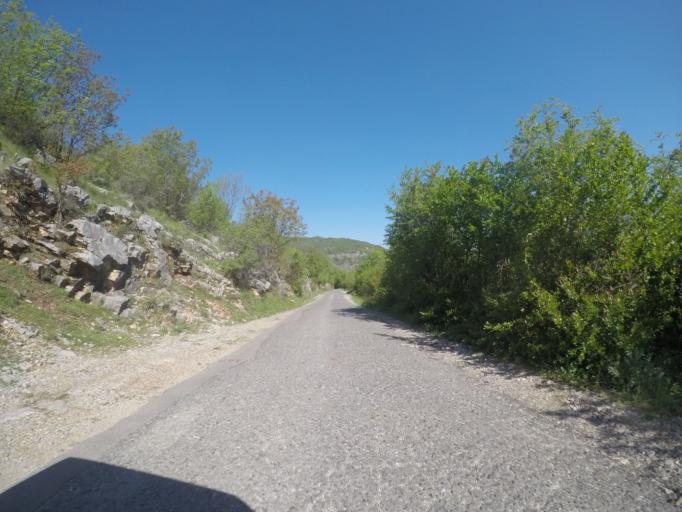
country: ME
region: Danilovgrad
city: Danilovgrad
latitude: 42.5288
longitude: 19.0929
